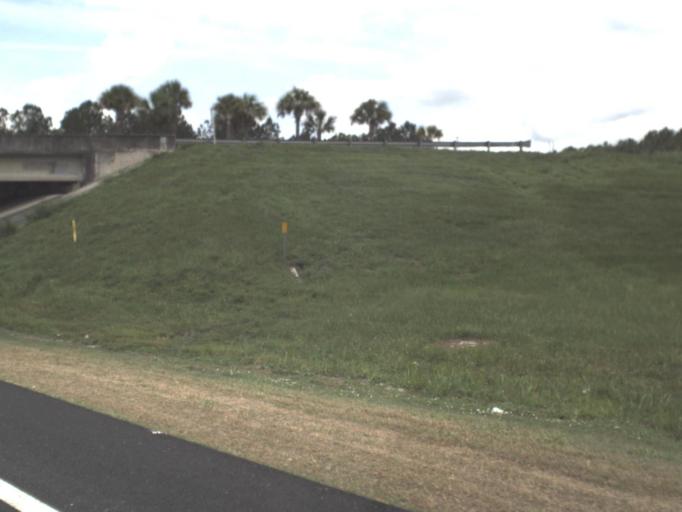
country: US
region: Florida
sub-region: Nassau County
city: Nassau Village-Ratliff
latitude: 30.4385
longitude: -81.7235
